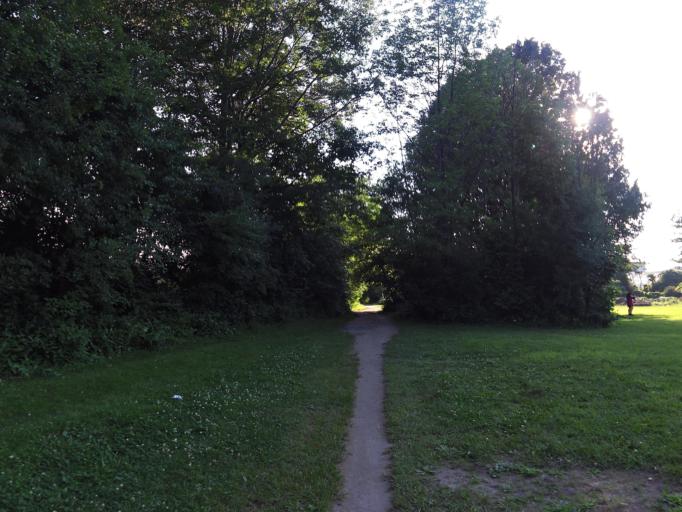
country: CA
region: Ontario
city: Ottawa
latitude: 45.3835
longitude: -75.6907
